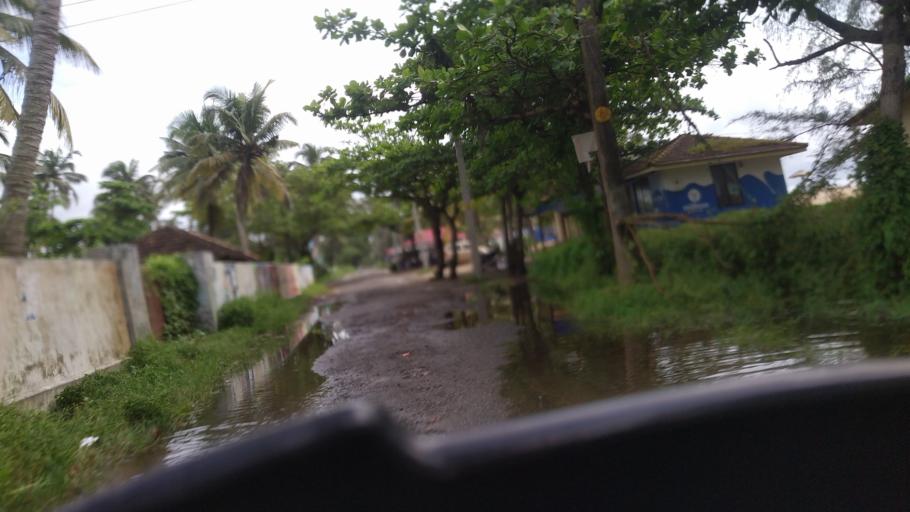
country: IN
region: Kerala
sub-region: Ernakulam
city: Elur
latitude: 10.1106
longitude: 76.1875
